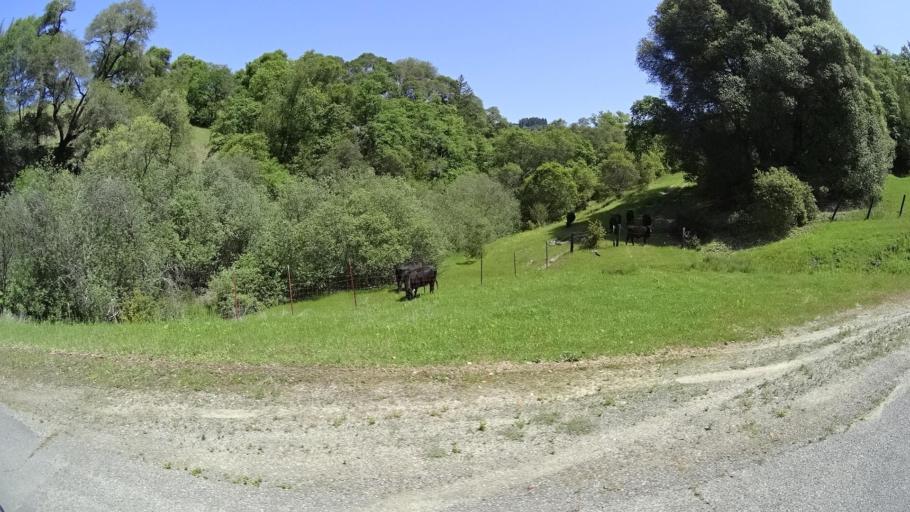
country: US
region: California
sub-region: Humboldt County
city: Redway
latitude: 40.2051
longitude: -123.5923
